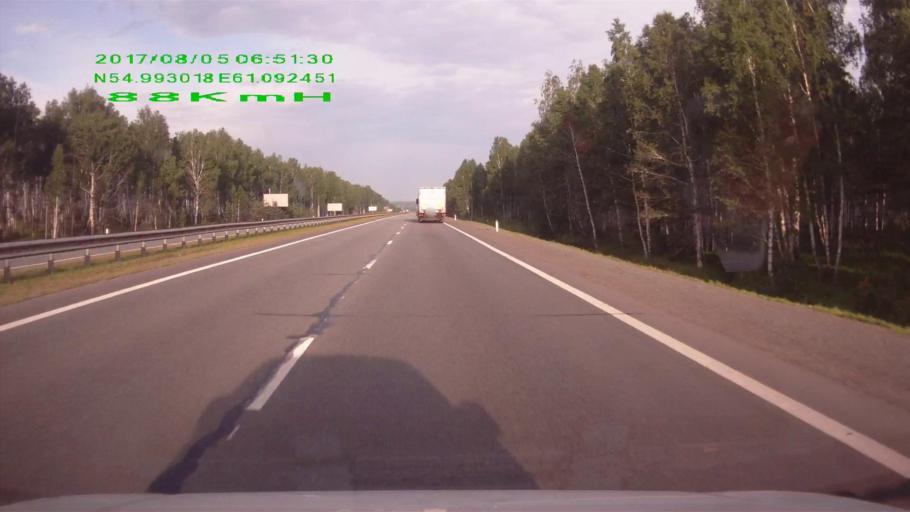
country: RU
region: Chelyabinsk
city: Poletayevo
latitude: 54.9930
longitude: 61.0922
